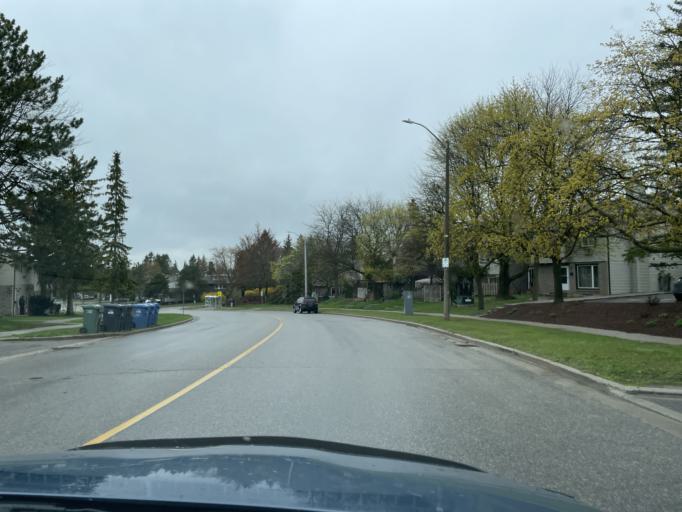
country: CA
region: Ontario
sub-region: Wellington County
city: Guelph
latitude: 43.5201
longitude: -80.2390
